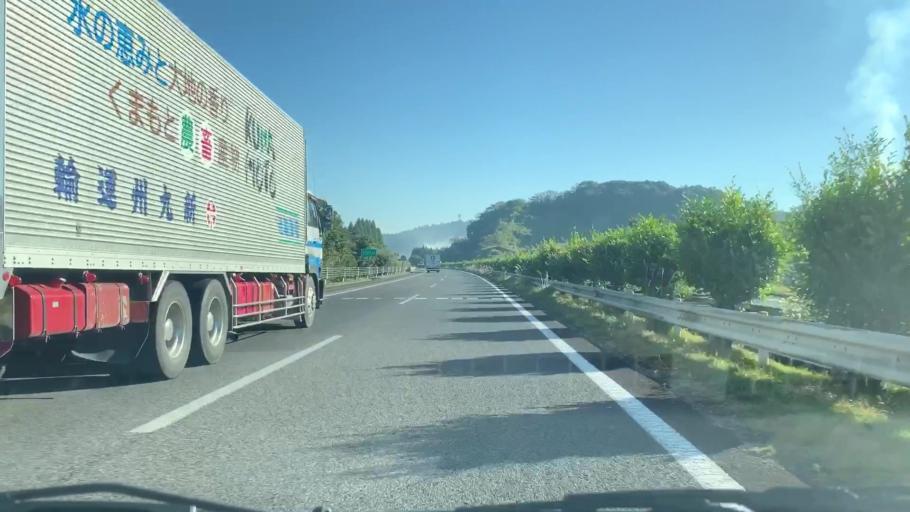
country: JP
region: Saga Prefecture
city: Takeocho-takeo
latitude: 33.2719
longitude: 130.1045
